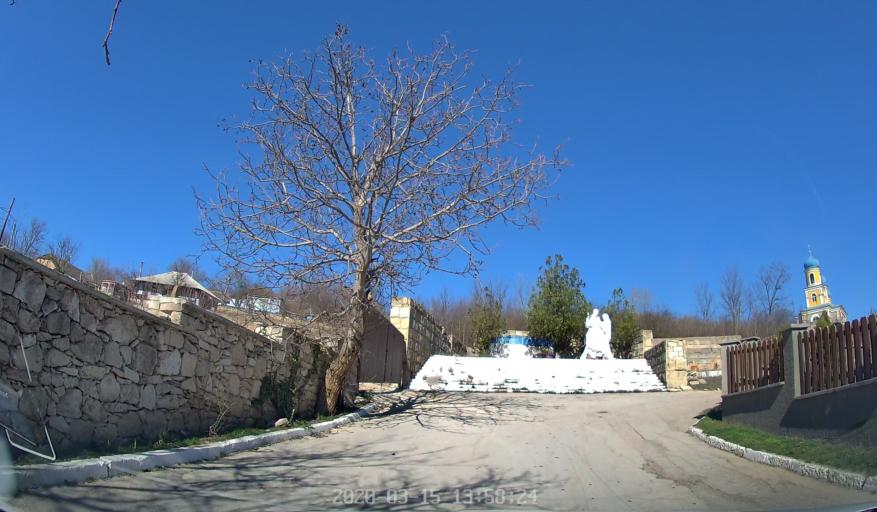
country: MD
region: Telenesti
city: Cocieri
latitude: 47.3121
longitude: 28.9749
